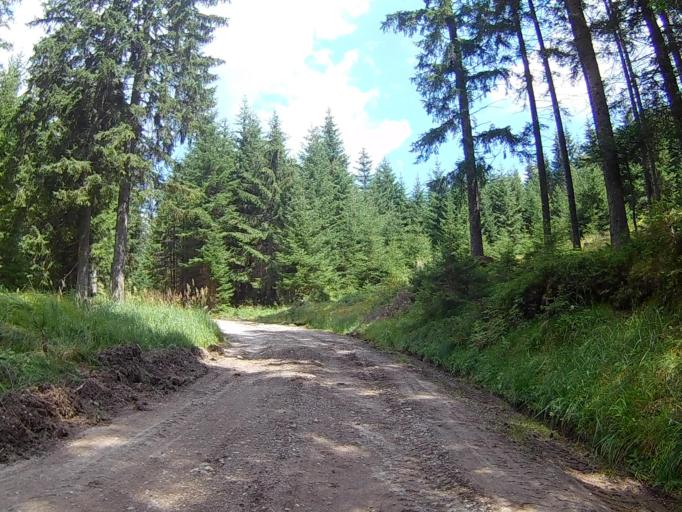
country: SI
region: Lovrenc na Pohorju
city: Lovrenc na Pohorju
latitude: 46.4819
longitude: 15.4402
